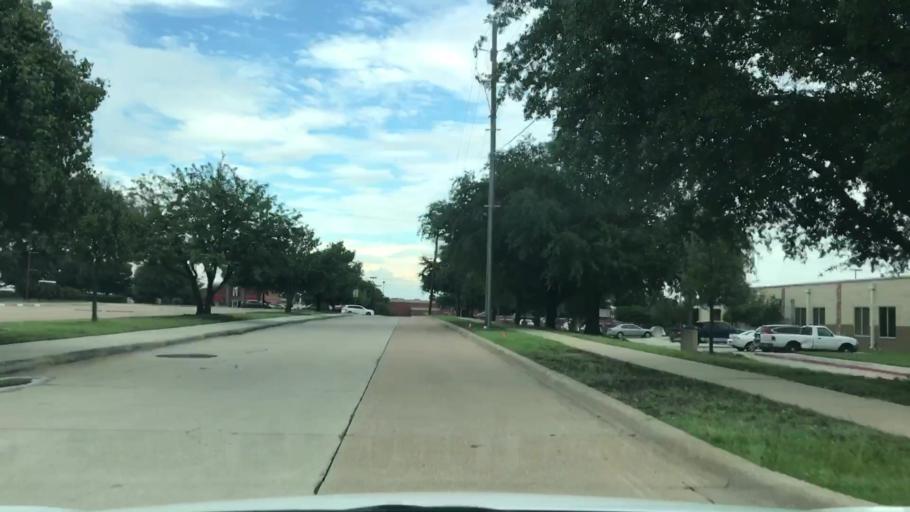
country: US
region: Texas
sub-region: Collin County
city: Frisco
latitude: 33.1408
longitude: -96.8061
